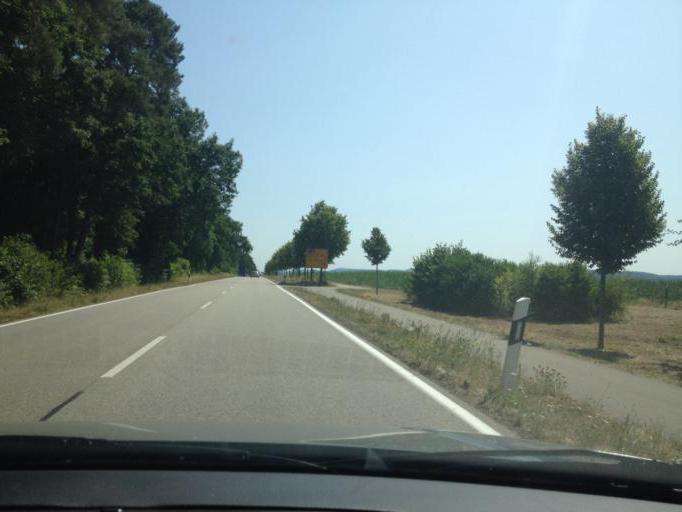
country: DE
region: Rheinland-Pfalz
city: Gries
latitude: 49.4098
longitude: 7.4125
